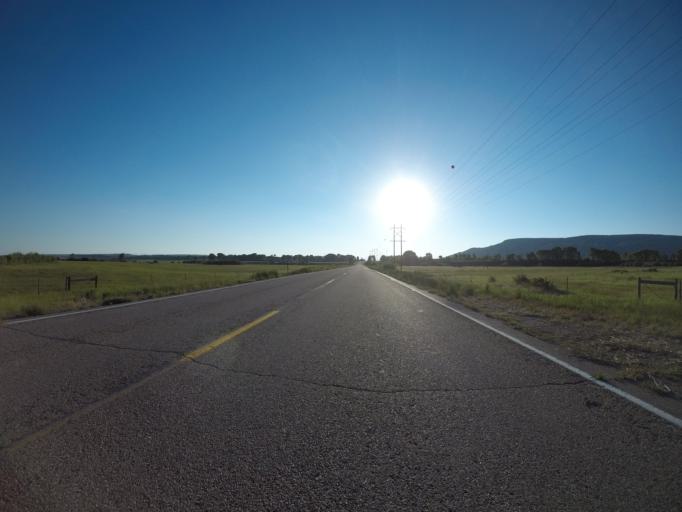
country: US
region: Wyoming
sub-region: Sublette County
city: Marbleton
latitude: 42.5735
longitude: -109.9409
